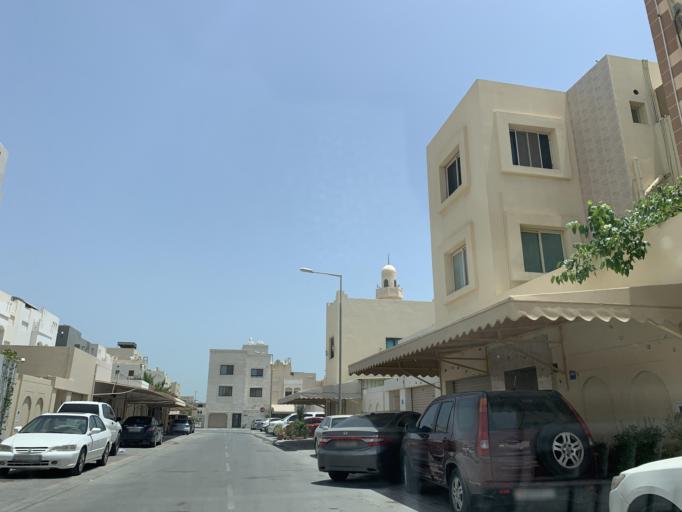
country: BH
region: Northern
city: Sitrah
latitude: 26.1385
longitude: 50.5909
